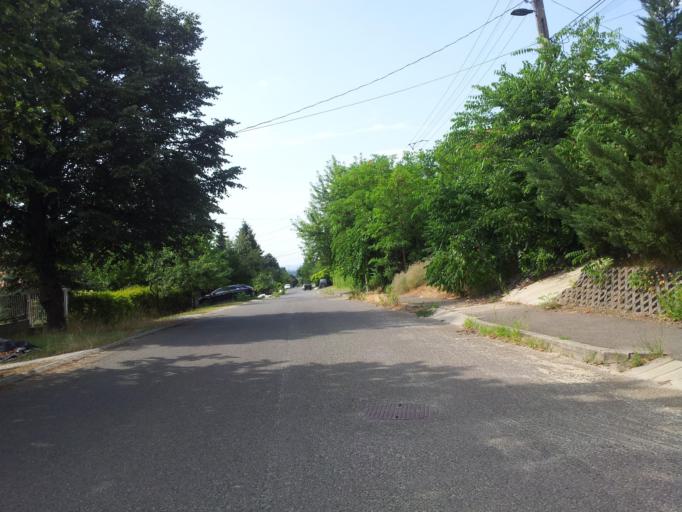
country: HU
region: Pest
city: Veresegyhaz
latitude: 47.6464
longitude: 19.3082
